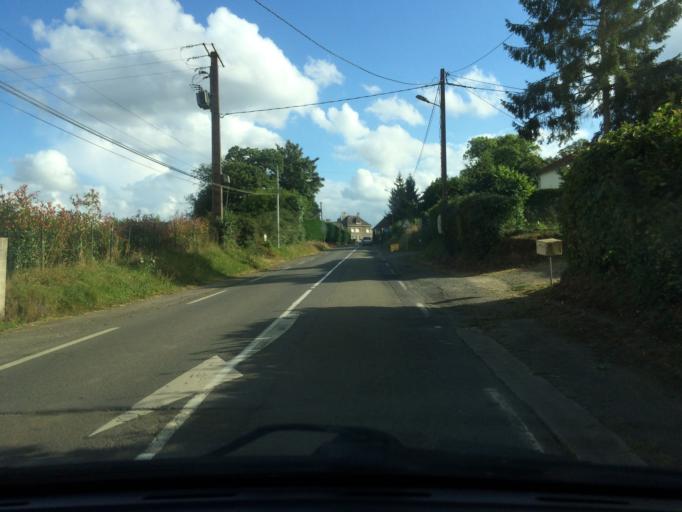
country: FR
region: Lower Normandy
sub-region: Departement du Calvados
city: Clecy
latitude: 48.8553
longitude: -0.4106
